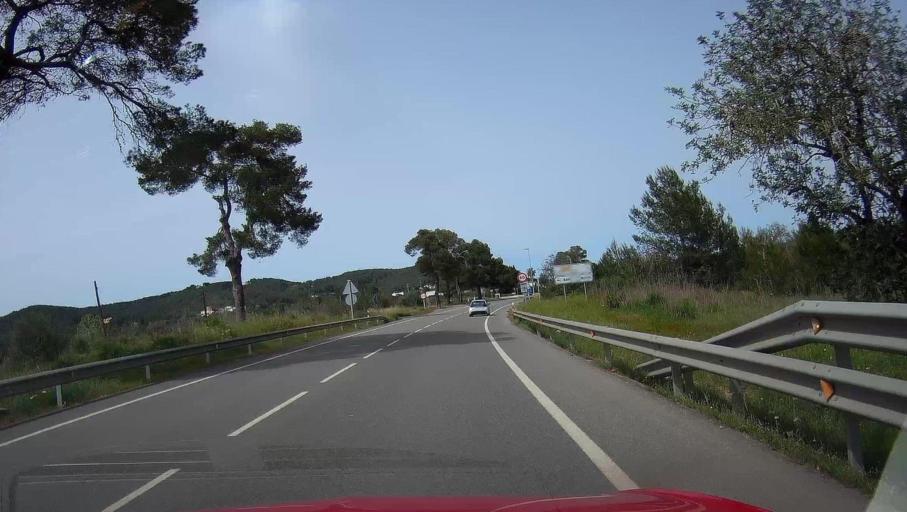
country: ES
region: Balearic Islands
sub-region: Illes Balears
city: Sant Joan de Labritja
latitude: 39.0252
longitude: 1.4870
